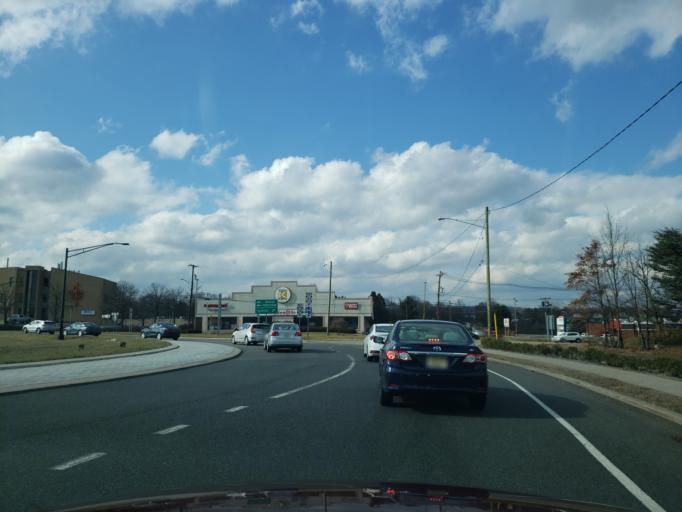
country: US
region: New Jersey
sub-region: Hunterdon County
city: Flemington
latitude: 40.5031
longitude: -74.8525
